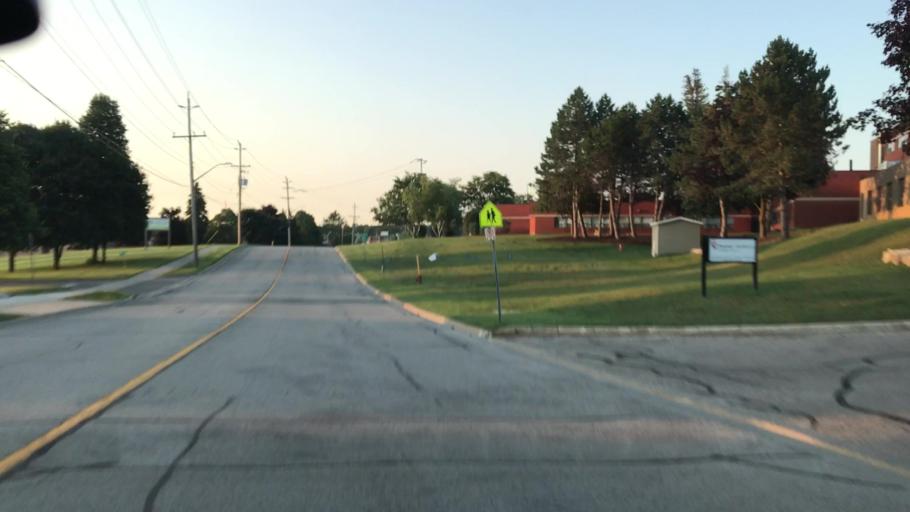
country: CA
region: Ontario
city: Newmarket
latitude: 44.0072
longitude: -79.4599
